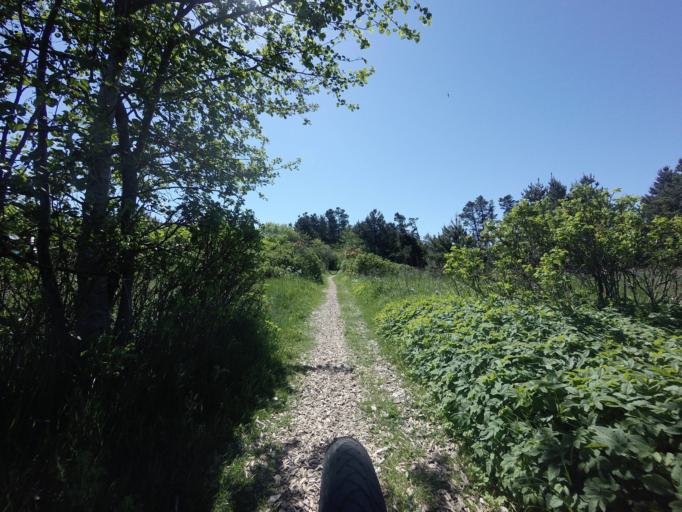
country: DK
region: North Denmark
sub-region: Jammerbugt Kommune
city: Pandrup
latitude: 57.2594
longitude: 9.6206
